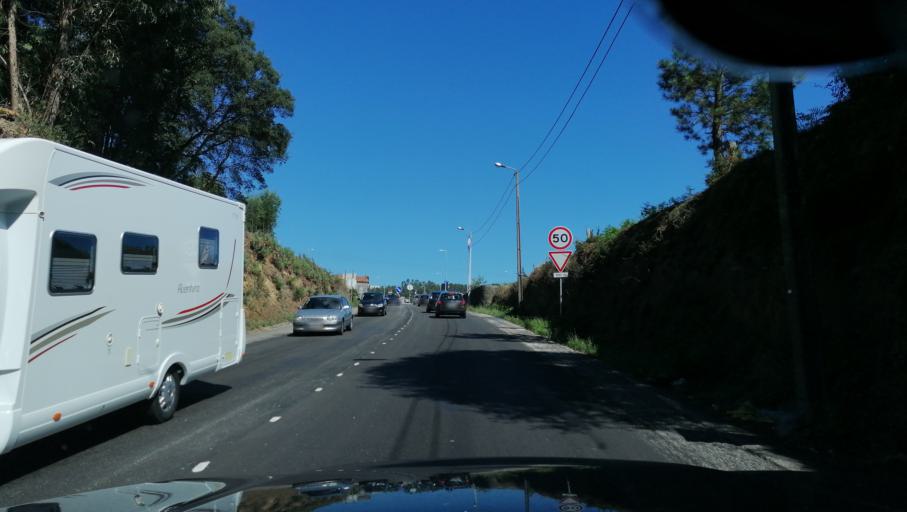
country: PT
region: Aveiro
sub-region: Santa Maria da Feira
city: Feira
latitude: 40.9303
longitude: -8.5184
